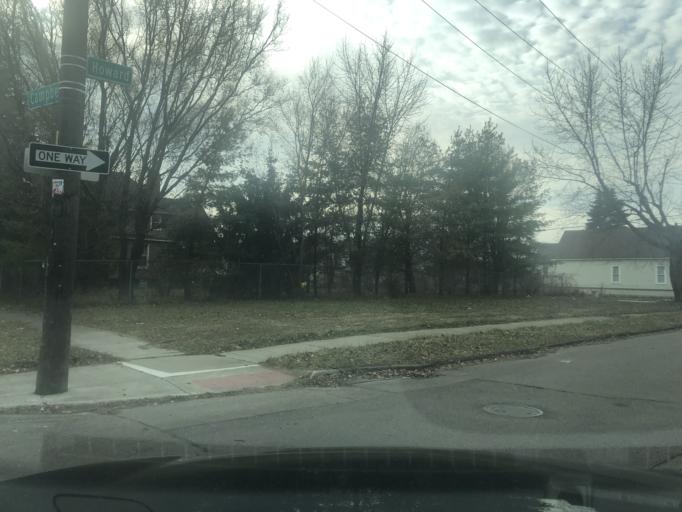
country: US
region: Michigan
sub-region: Wayne County
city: River Rouge
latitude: 42.3124
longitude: -83.1005
